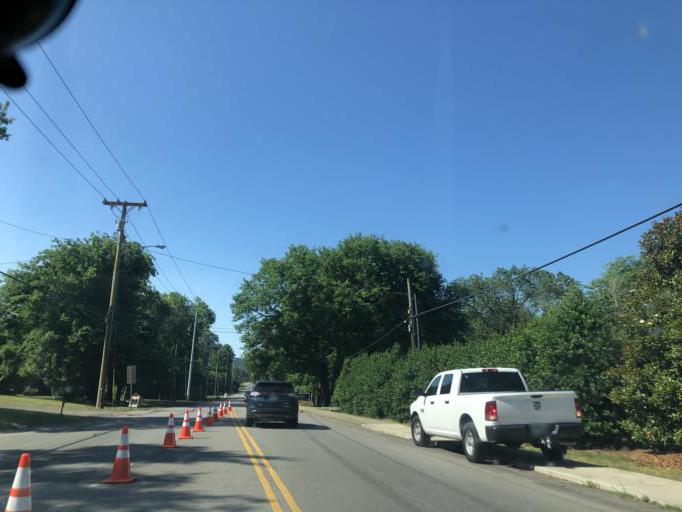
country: US
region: Tennessee
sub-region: Davidson County
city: Oak Hill
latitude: 36.1127
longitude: -86.8001
